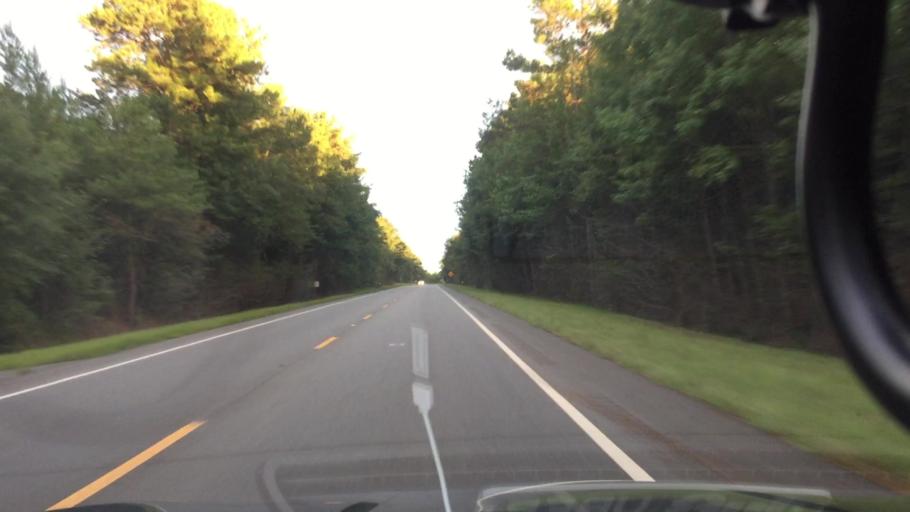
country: US
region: Alabama
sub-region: Pike County
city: Brundidge
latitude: 31.5818
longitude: -85.9351
